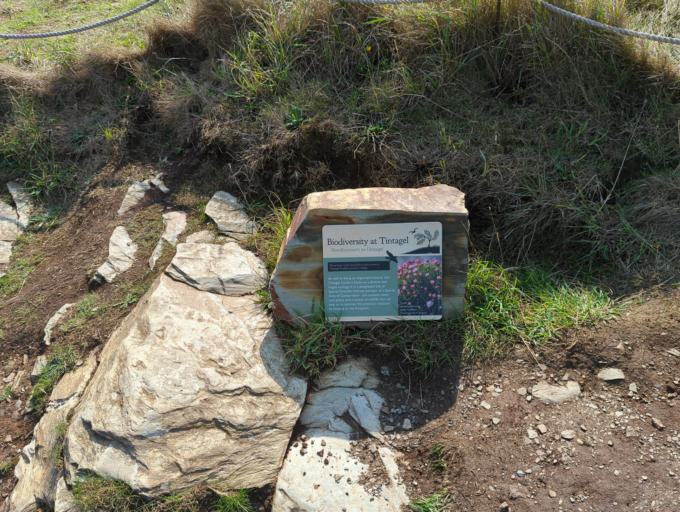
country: GB
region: England
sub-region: Cornwall
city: Tintagel
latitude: 50.6691
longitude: -4.7610
